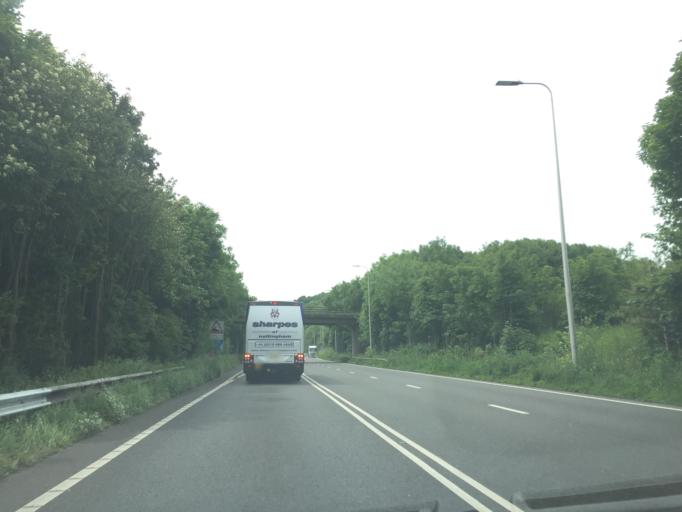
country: GB
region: England
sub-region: Kent
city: Dover
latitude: 51.1343
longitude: 1.3304
